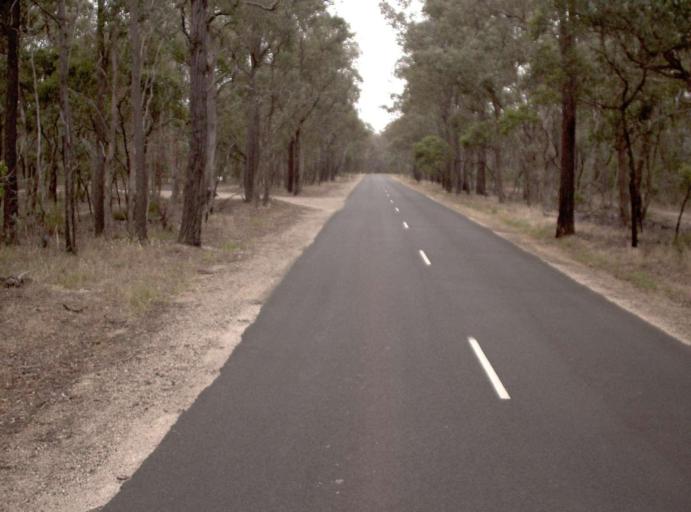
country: AU
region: Victoria
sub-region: Wellington
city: Heyfield
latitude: -37.9551
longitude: 146.7705
